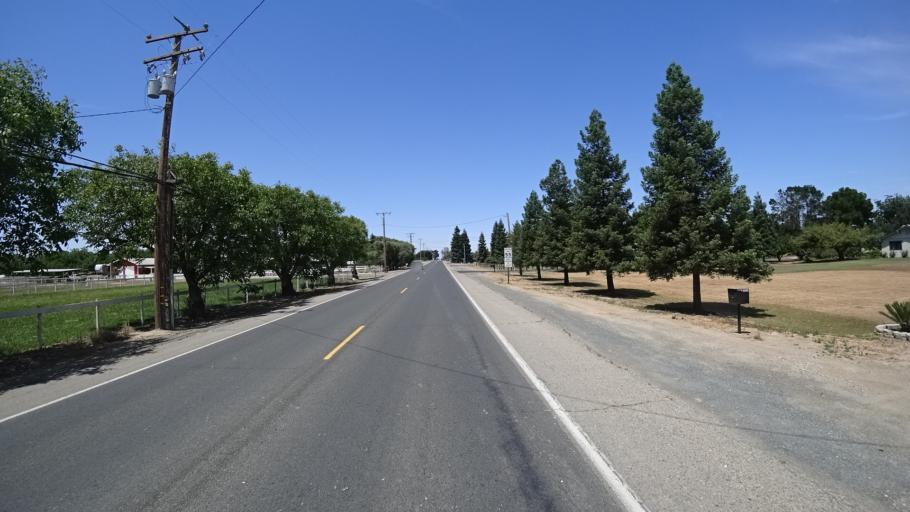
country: US
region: California
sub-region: Kings County
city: Armona
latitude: 36.3426
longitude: -119.7136
